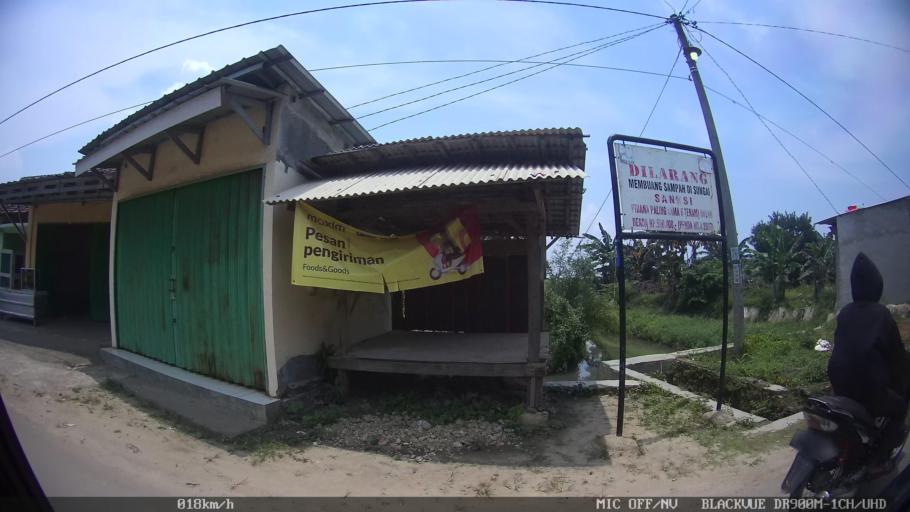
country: ID
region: Lampung
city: Kedaton
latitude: -5.3382
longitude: 105.2477
